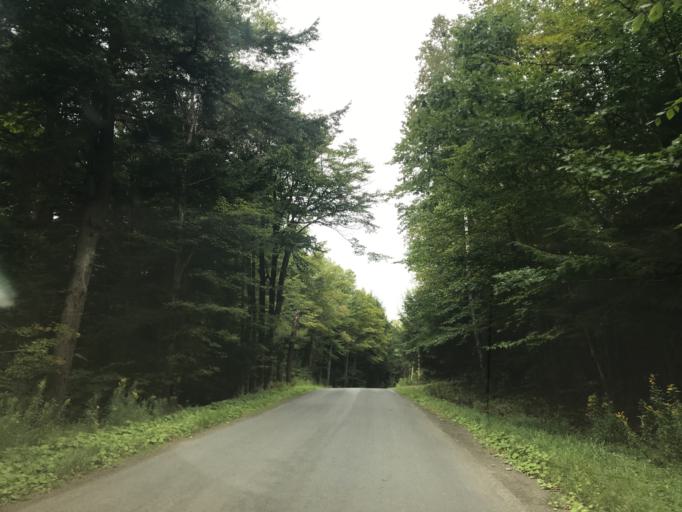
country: US
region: New York
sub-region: Otsego County
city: Worcester
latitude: 42.5877
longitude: -74.6787
